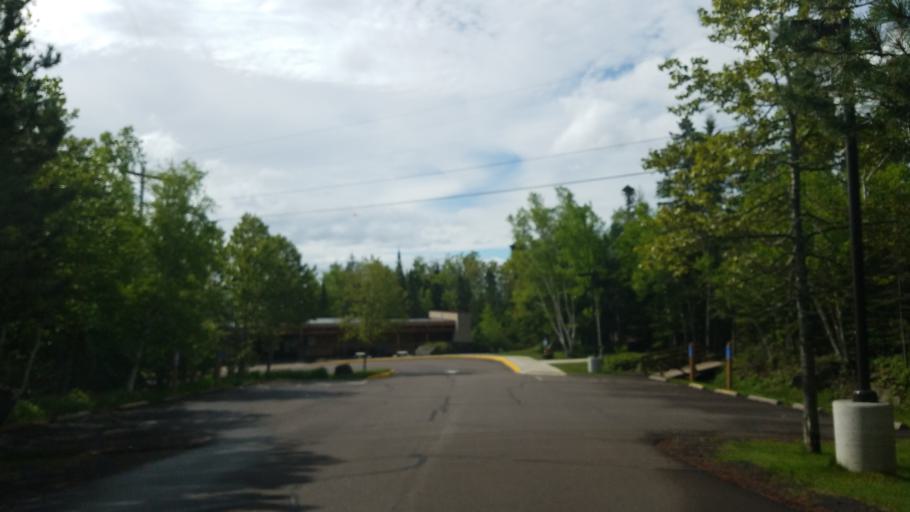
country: US
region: Minnesota
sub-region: Lake County
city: Silver Bay
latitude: 47.2016
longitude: -91.3677
